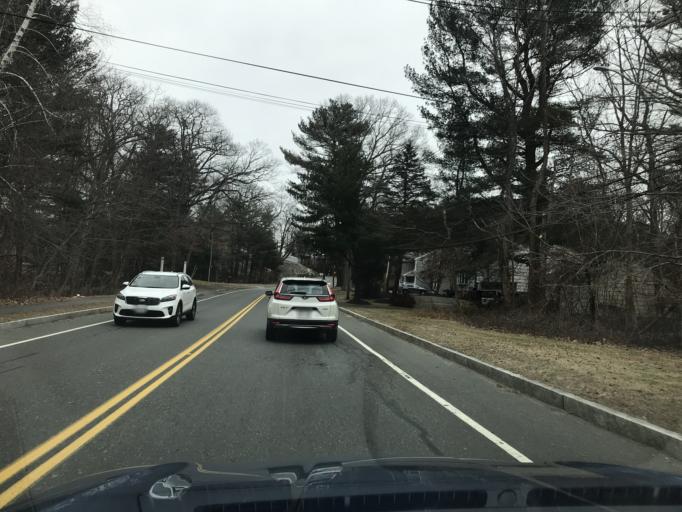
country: US
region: Massachusetts
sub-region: Essex County
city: Lynnfield
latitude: 42.5124
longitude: -71.0203
